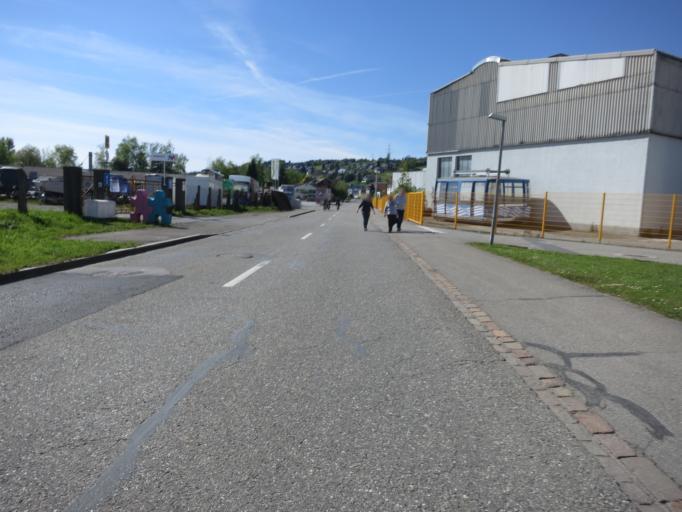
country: CH
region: Saint Gallen
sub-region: Wahlkreis See-Gaster
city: Schmerikon
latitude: 47.2234
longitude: 8.9521
